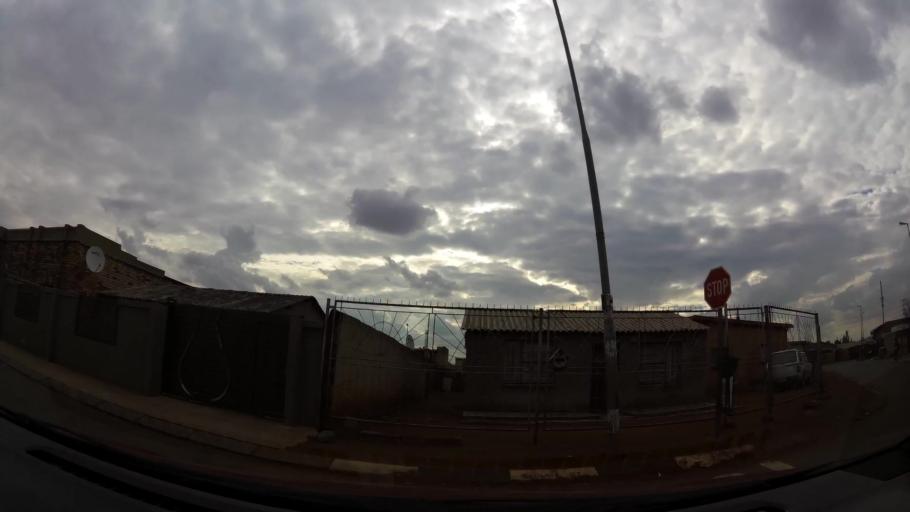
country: ZA
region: Gauteng
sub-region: City of Johannesburg Metropolitan Municipality
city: Soweto
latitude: -26.2465
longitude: 27.8446
